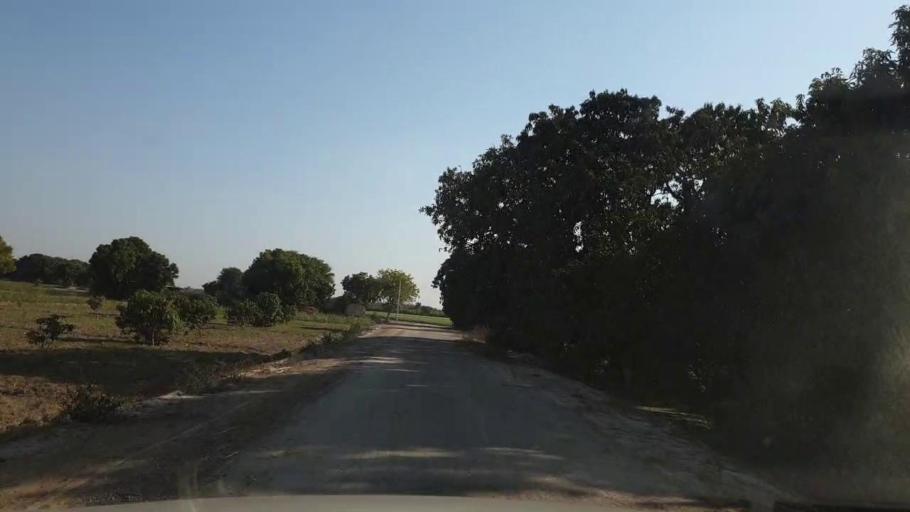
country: PK
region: Sindh
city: Tando Allahyar
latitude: 25.4919
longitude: 68.6451
